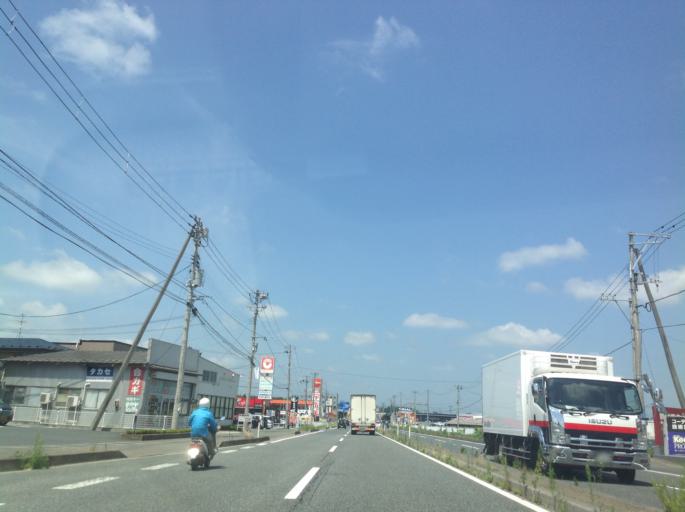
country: JP
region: Iwate
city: Kitakami
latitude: 39.3317
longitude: 141.1099
